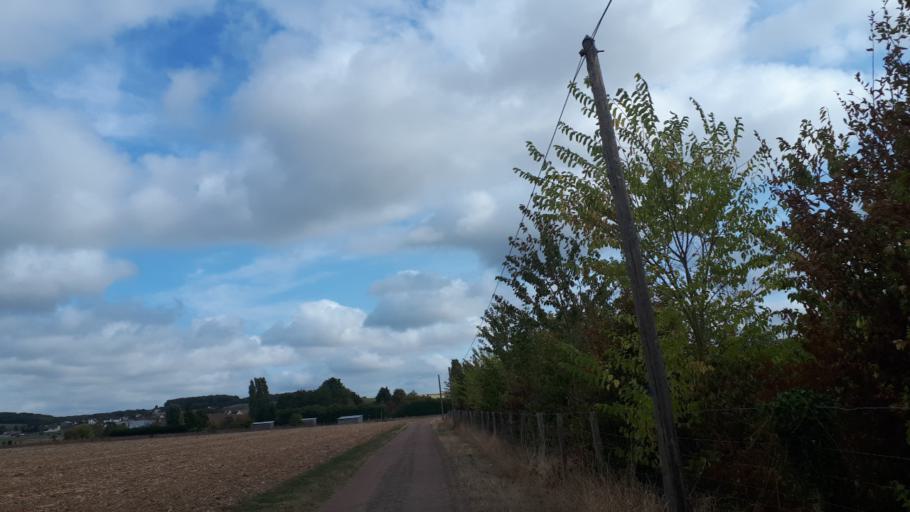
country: FR
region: Centre
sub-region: Departement du Loir-et-Cher
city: Villiers-sur-Loir
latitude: 47.7907
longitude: 0.9935
